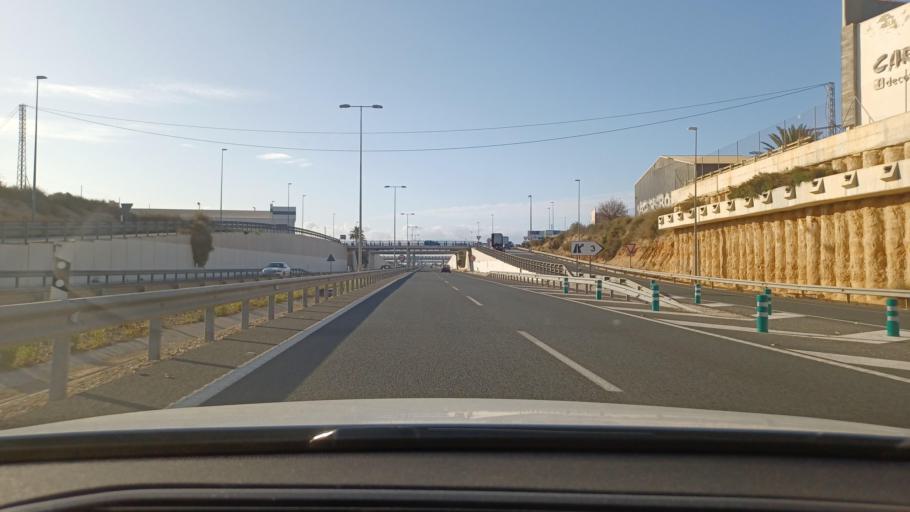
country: ES
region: Valencia
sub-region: Provincia de Alicante
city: Elche
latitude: 38.2769
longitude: -0.6618
